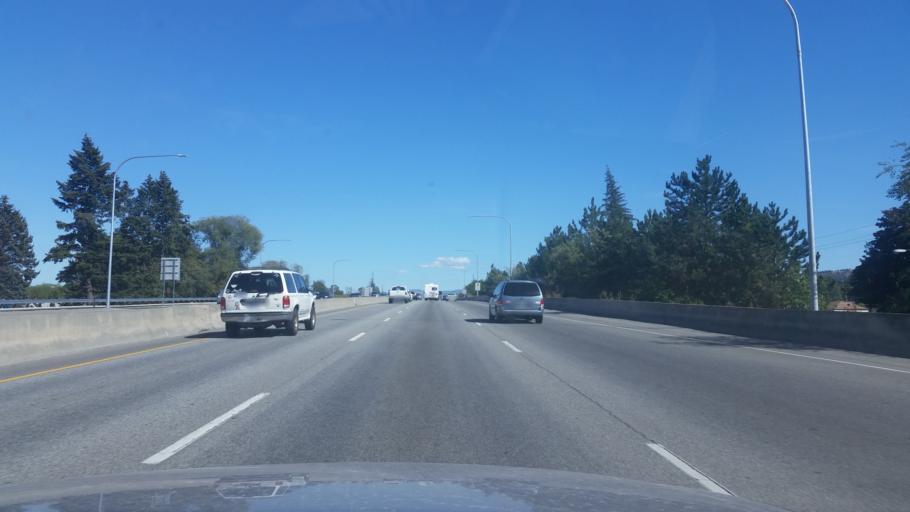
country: US
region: Washington
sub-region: Spokane County
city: Millwood
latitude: 47.6538
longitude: -117.3530
